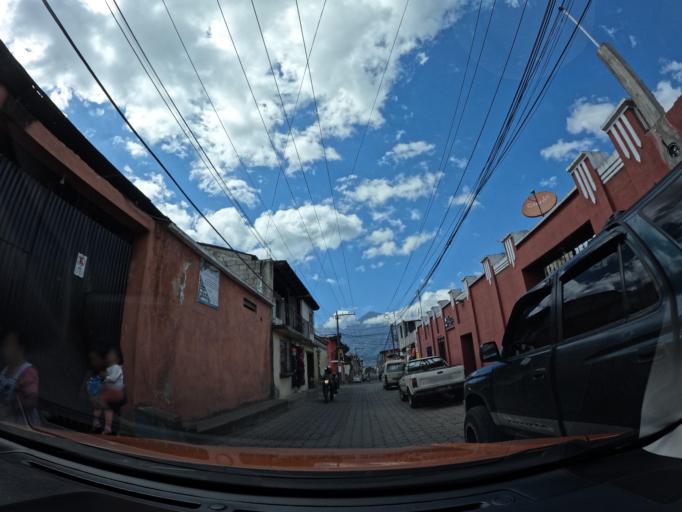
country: GT
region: Sacatepequez
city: Ciudad Vieja
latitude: 14.5259
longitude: -90.7535
